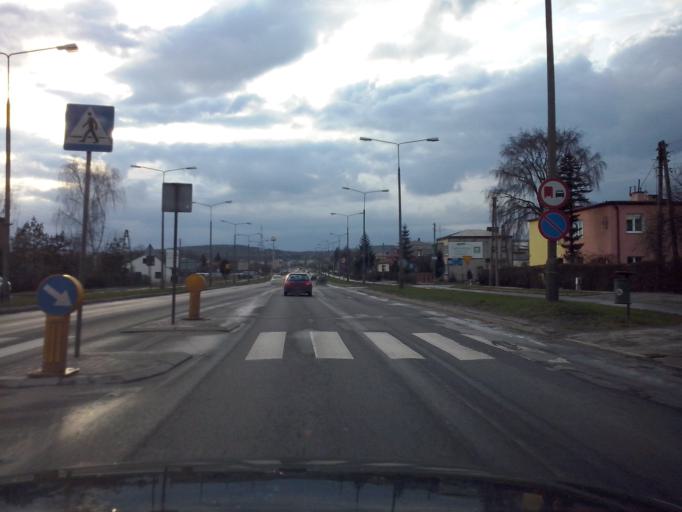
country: PL
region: Lublin Voivodeship
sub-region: Chelm
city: Chelm
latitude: 51.1455
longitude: 23.4477
